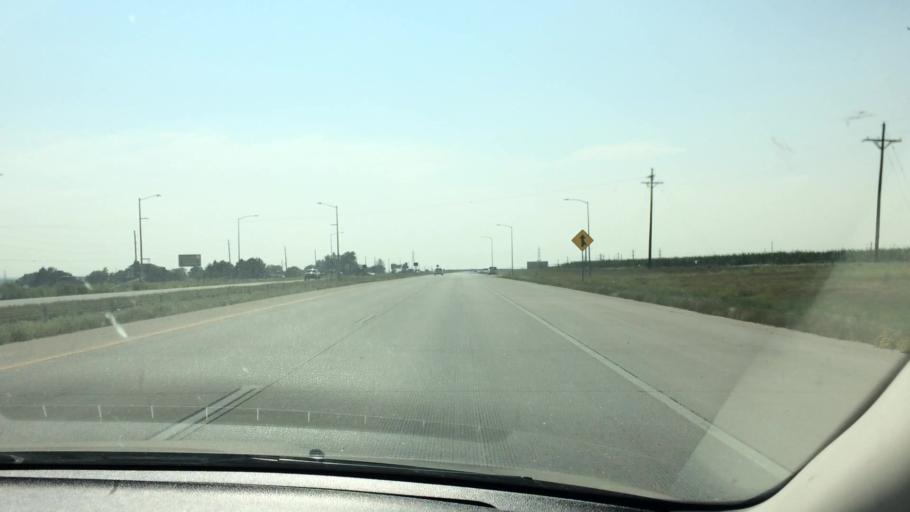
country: US
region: Colorado
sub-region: Adams County
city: Aurora
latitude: 39.7404
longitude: -104.6631
